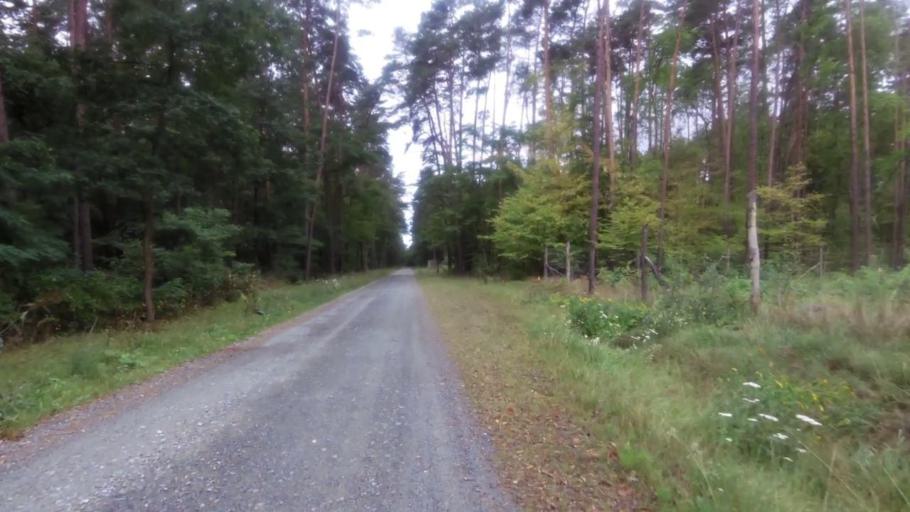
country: PL
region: West Pomeranian Voivodeship
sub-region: Powiat mysliborski
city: Debno
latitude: 52.7080
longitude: 14.6585
